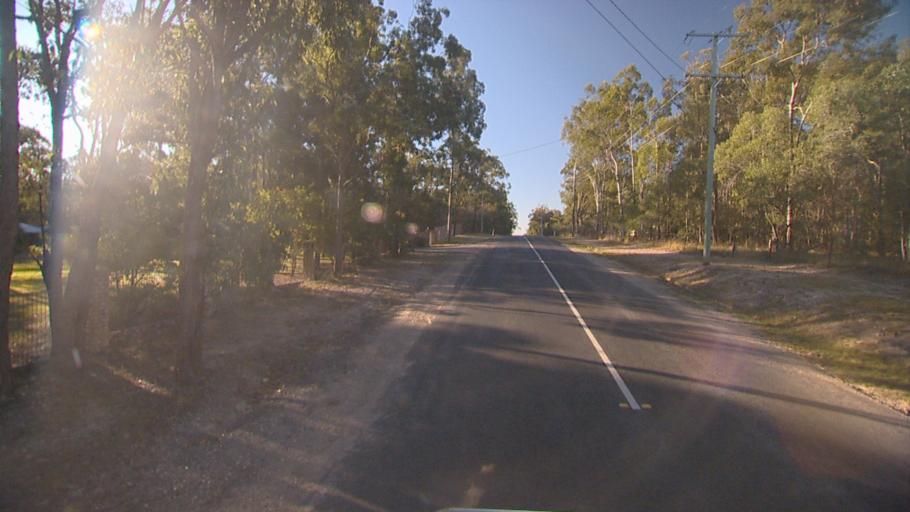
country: AU
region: Queensland
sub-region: Logan
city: Chambers Flat
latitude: -27.7687
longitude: 153.1378
